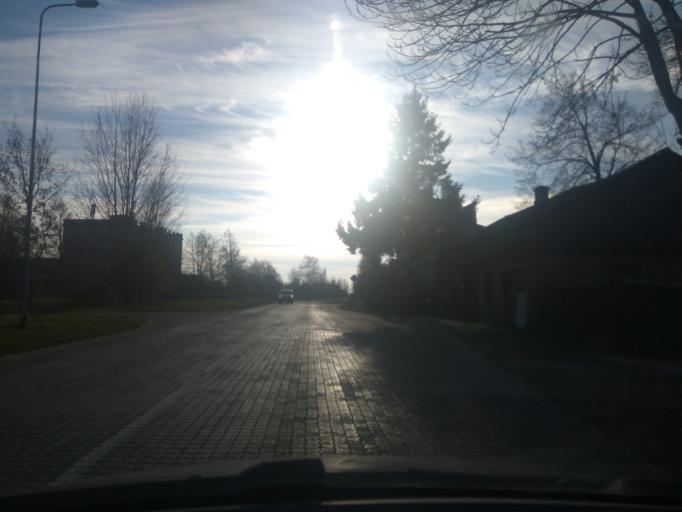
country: LV
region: Ventspils
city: Ventspils
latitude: 57.3717
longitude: 21.5694
